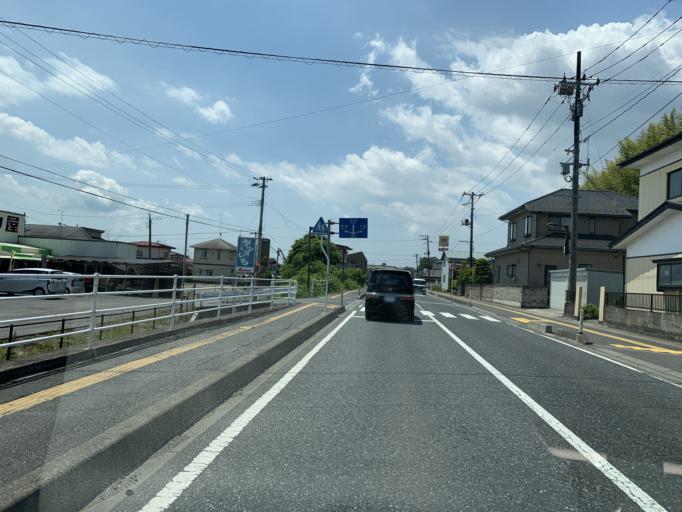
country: JP
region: Miyagi
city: Wakuya
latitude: 38.4686
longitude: 141.0944
